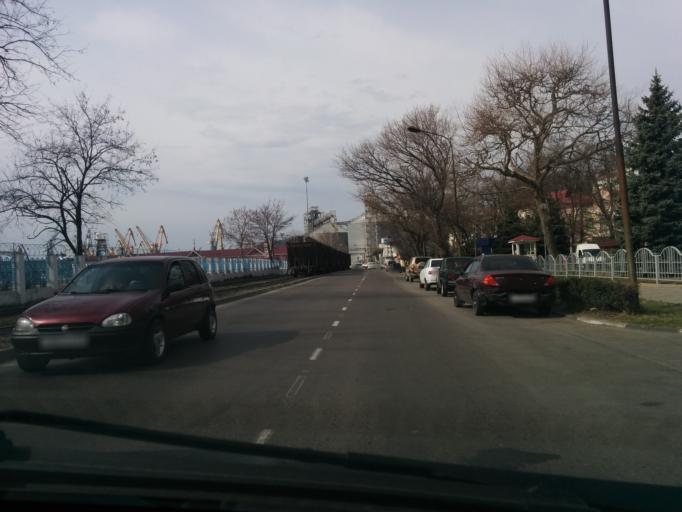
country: RU
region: Krasnodarskiy
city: Tuapse
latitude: 44.0949
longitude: 39.0715
